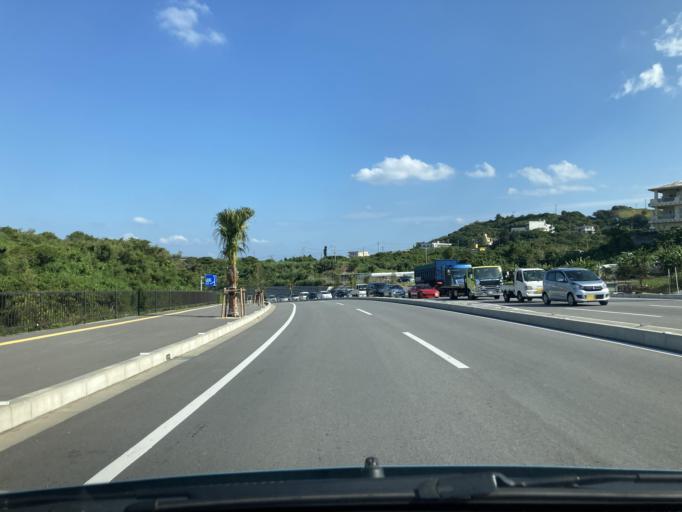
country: JP
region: Okinawa
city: Chatan
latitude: 26.2989
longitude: 127.7983
